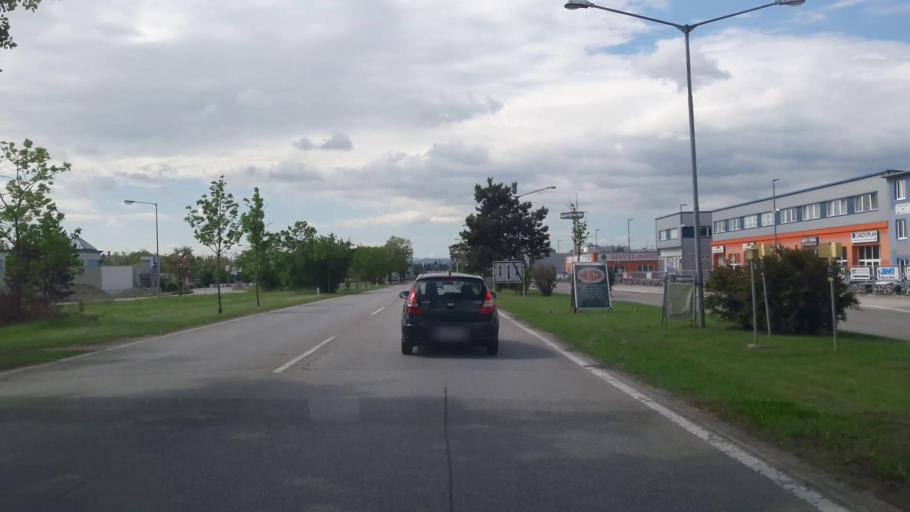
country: AT
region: Lower Austria
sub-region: Politischer Bezirk Wiener Neustadt
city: Theresienfeld
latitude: 47.8371
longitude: 16.2451
